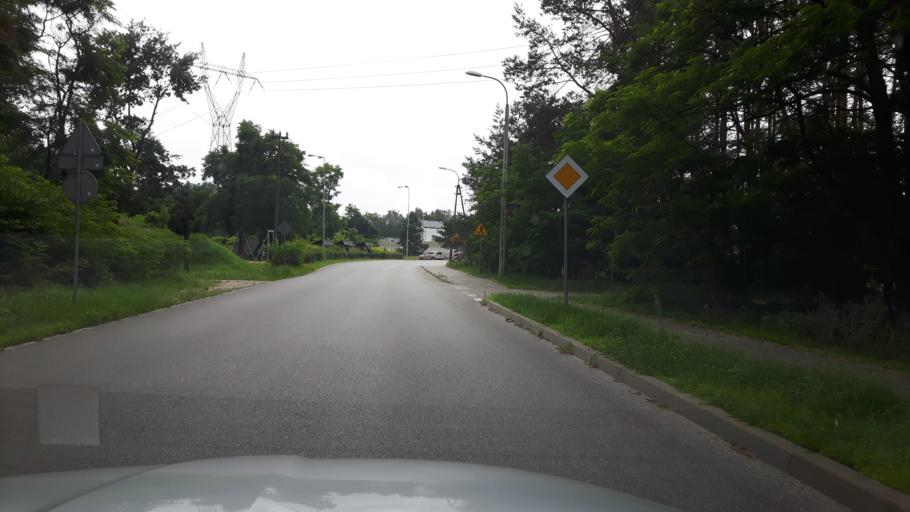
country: PL
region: Masovian Voivodeship
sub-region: Warszawa
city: Rembertow
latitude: 52.2784
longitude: 21.1712
